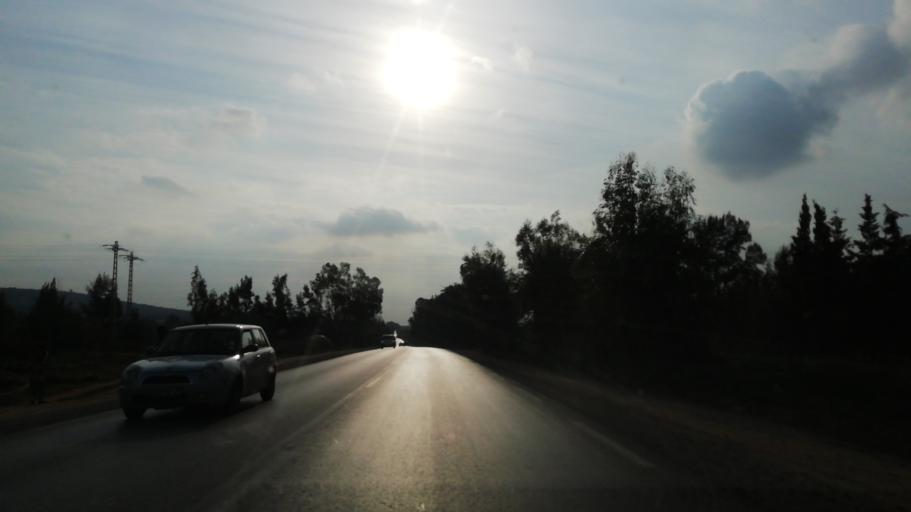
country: DZ
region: Mostaganem
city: Mostaganem
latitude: 35.8397
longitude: 0.0631
